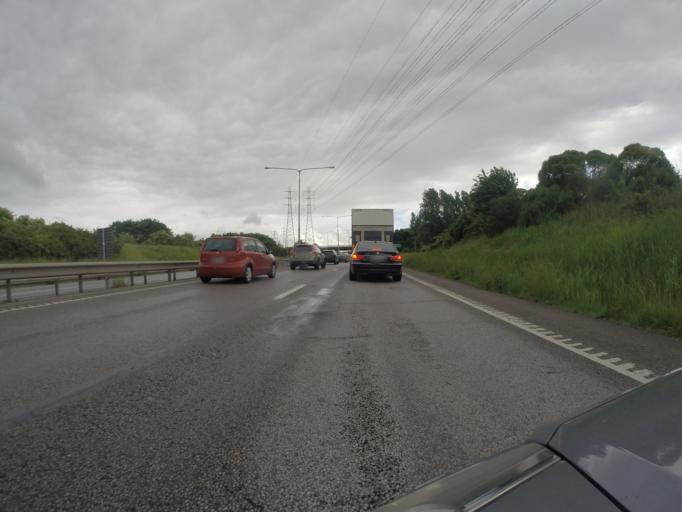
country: SE
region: Skane
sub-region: Burlovs Kommun
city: Arloev
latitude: 55.6242
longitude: 13.0566
